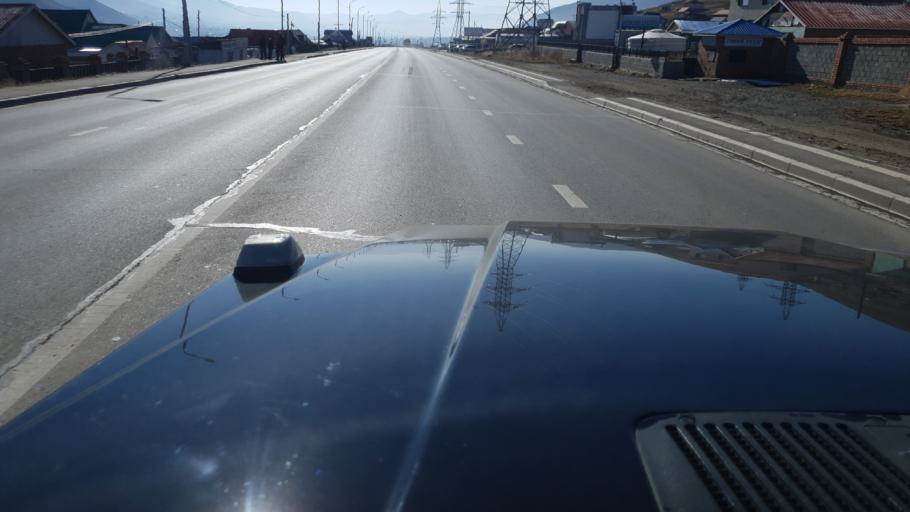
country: MN
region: Ulaanbaatar
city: Ulaanbaatar
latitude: 48.0324
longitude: 106.9090
